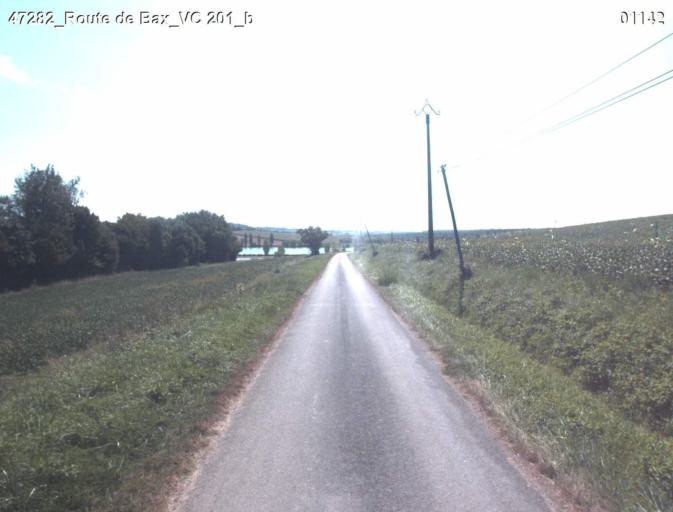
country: FR
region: Aquitaine
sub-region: Departement du Lot-et-Garonne
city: Laplume
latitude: 44.0783
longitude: 0.4958
